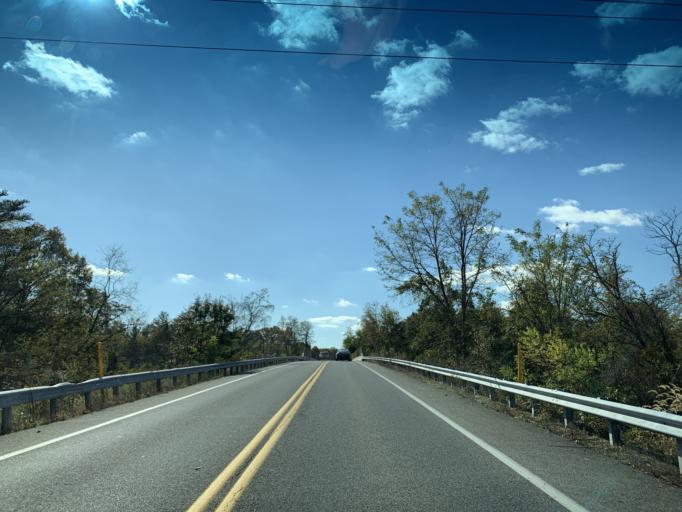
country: US
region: Maryland
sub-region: Anne Arundel County
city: Gambrills
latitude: 39.0762
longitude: -76.6613
